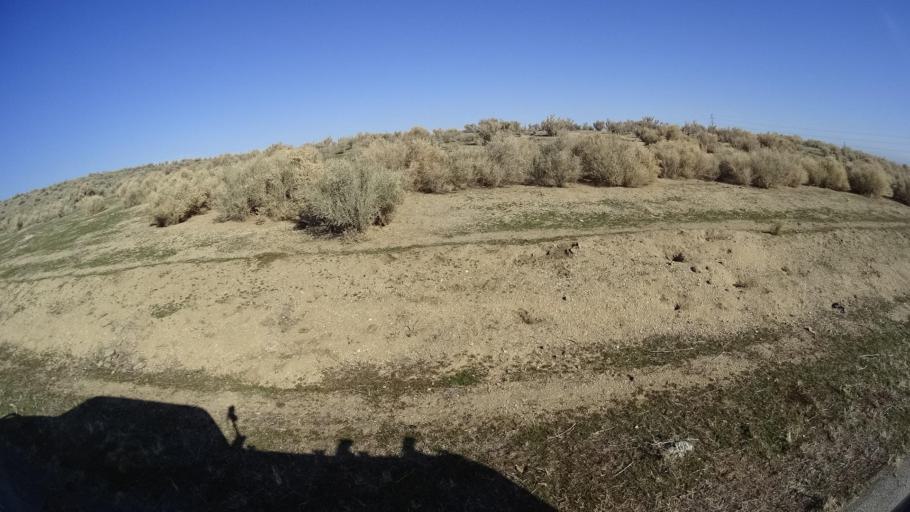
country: US
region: California
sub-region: Kern County
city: Taft Heights
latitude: 35.2278
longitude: -119.6367
